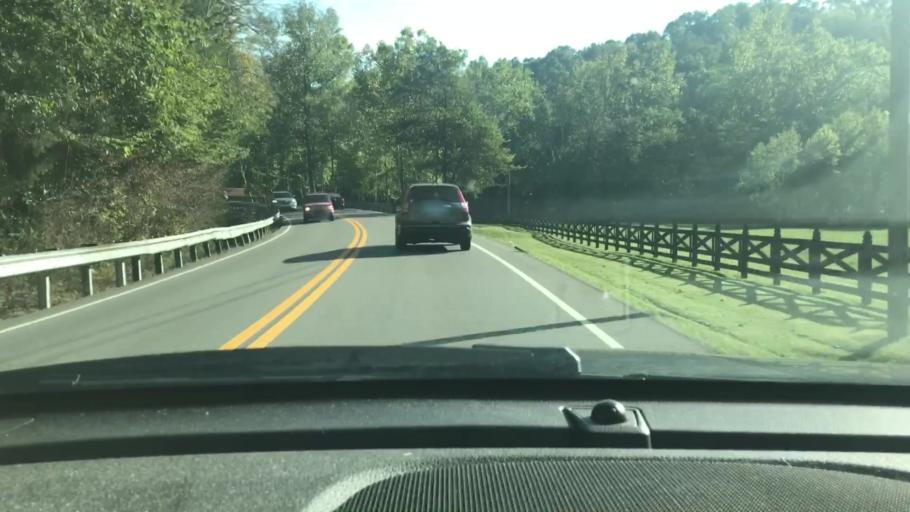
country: US
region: Tennessee
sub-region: Sumner County
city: White House
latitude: 36.4260
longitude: -86.6592
